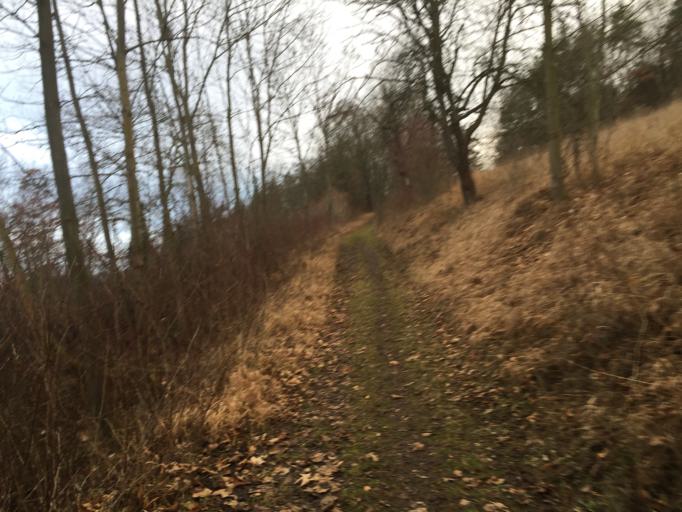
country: DE
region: Thuringia
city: Bad Blankenburg
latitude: 50.6972
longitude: 11.2581
